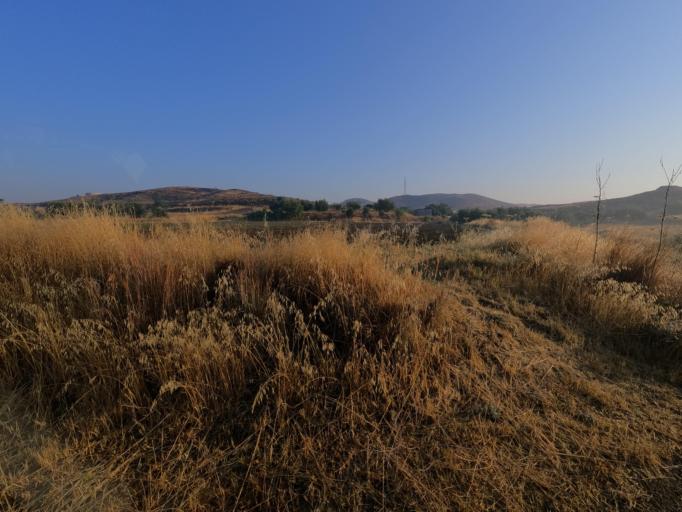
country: CY
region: Larnaka
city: Mosfiloti
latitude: 34.9731
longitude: 33.4257
